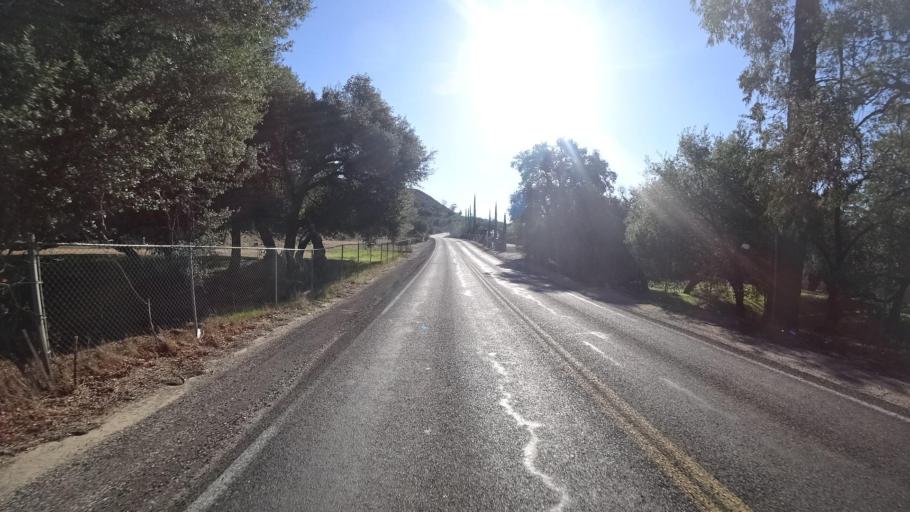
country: MX
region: Baja California
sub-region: Tijuana
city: Villa del Campo
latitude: 32.6240
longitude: -116.7514
